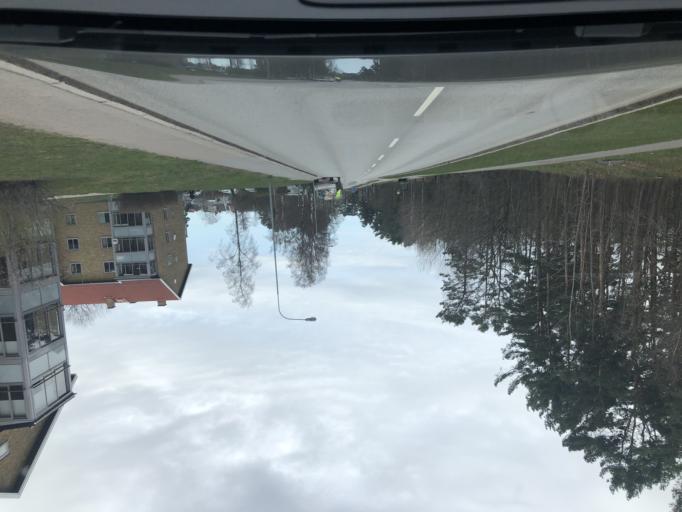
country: SE
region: Kalmar
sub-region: Kalmar Kommun
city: Kalmar
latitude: 56.6613
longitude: 16.3227
